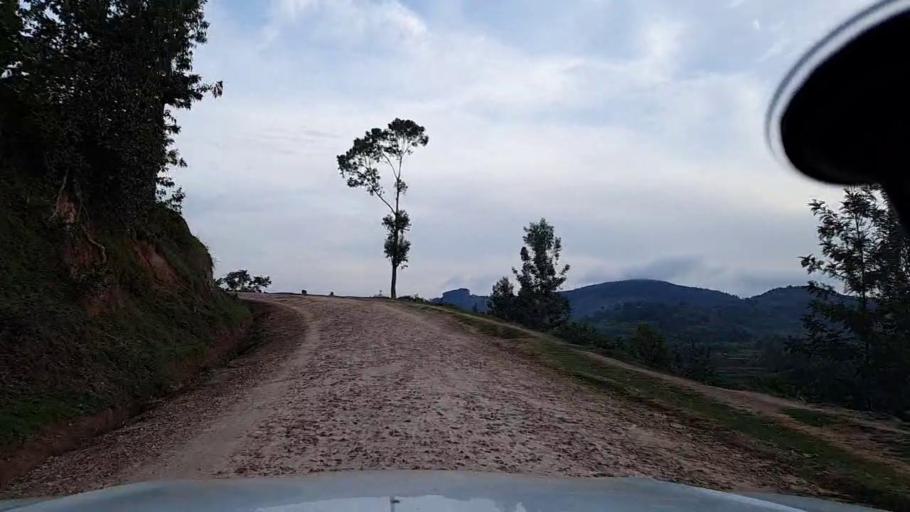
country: RW
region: Southern Province
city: Nyanza
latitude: -2.2210
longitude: 29.6459
